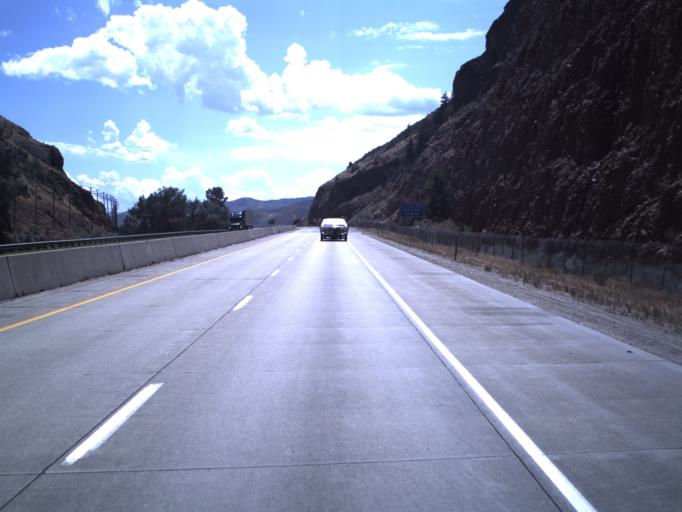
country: US
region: Utah
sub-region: Morgan County
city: Morgan
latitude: 41.0517
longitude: -111.5294
